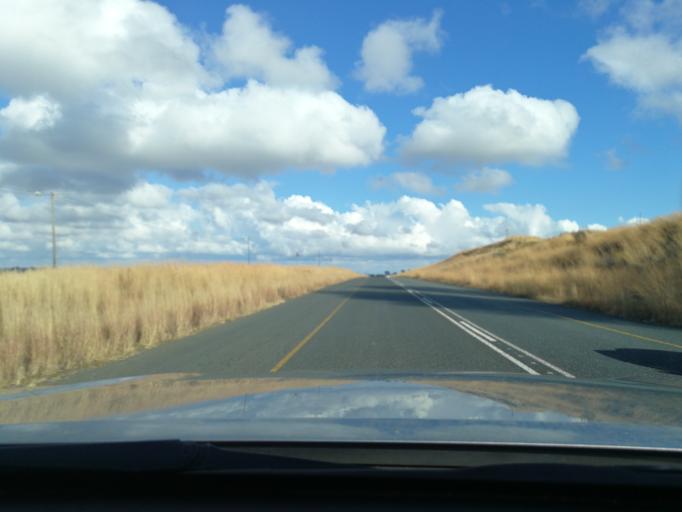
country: ZA
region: Orange Free State
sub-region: Thabo Mofutsanyana District Municipality
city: Reitz
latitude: -28.0031
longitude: 28.3768
